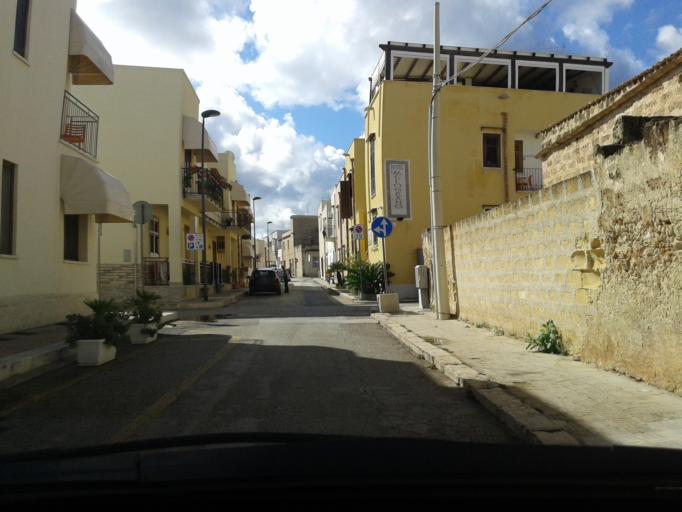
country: IT
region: Sicily
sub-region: Trapani
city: San Vito Lo Capo
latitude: 38.1744
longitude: 12.7381
